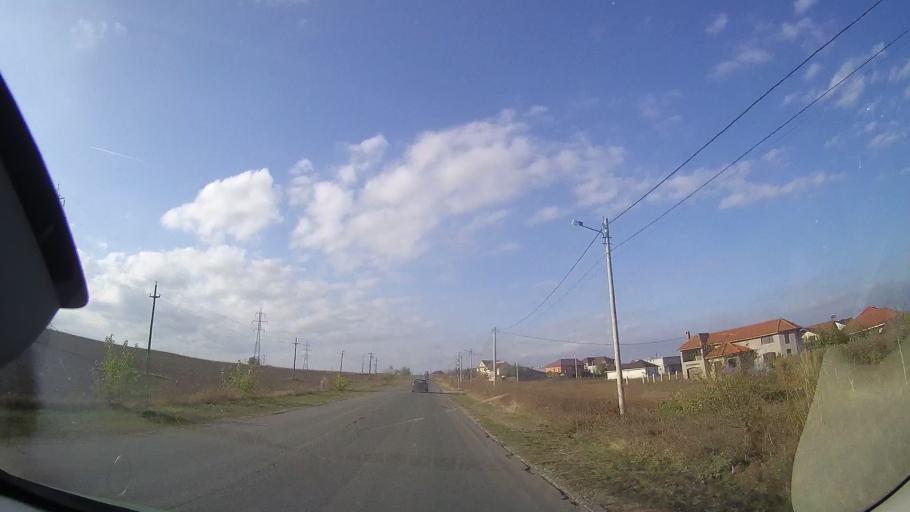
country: RO
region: Constanta
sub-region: Comuna Limanu
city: Limanu
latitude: 43.7916
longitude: 28.5475
